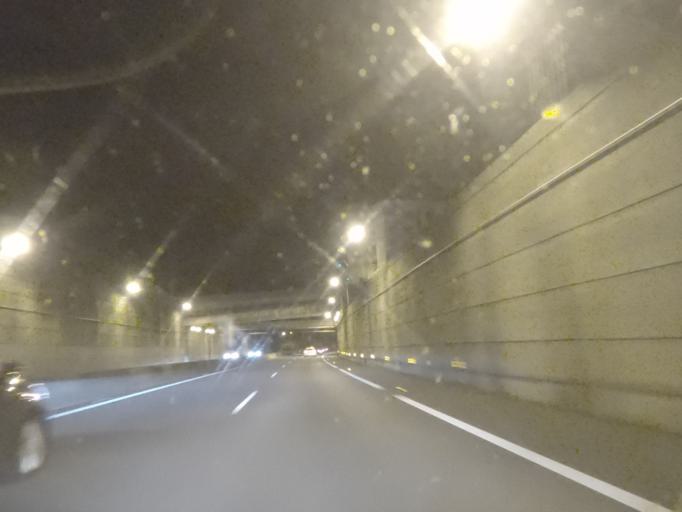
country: ES
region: Galicia
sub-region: Provincia da Coruna
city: Culleredo
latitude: 43.3134
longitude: -8.3818
